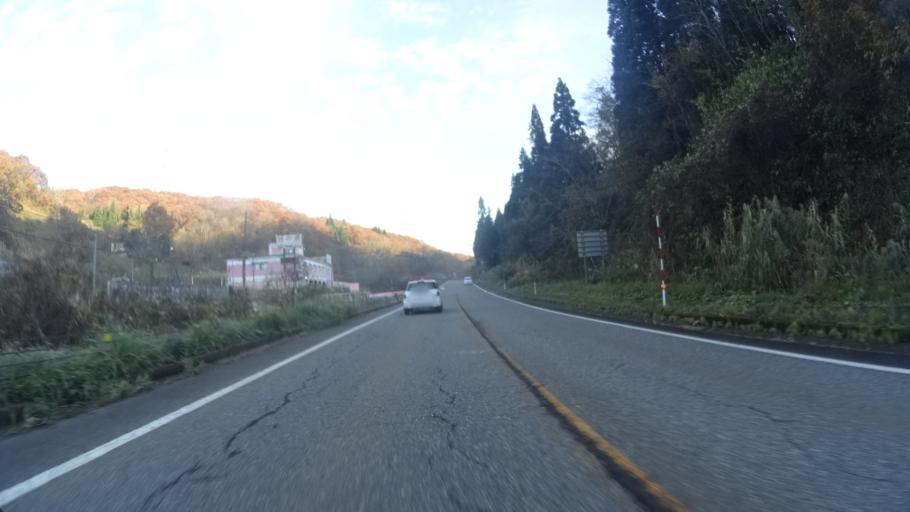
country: JP
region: Niigata
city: Kashiwazaki
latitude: 37.4129
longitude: 138.6825
